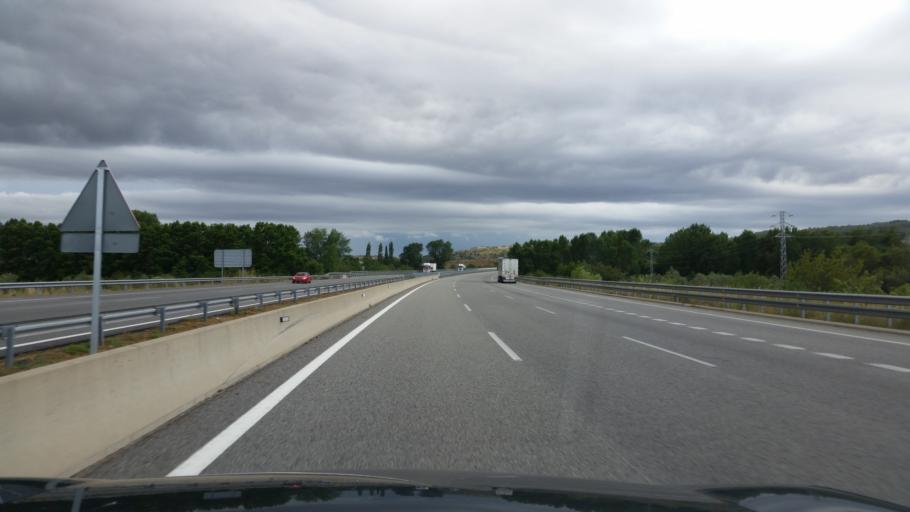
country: ES
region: Catalonia
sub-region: Provincia de Girona
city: Pont de Molins
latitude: 42.3060
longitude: 2.9458
